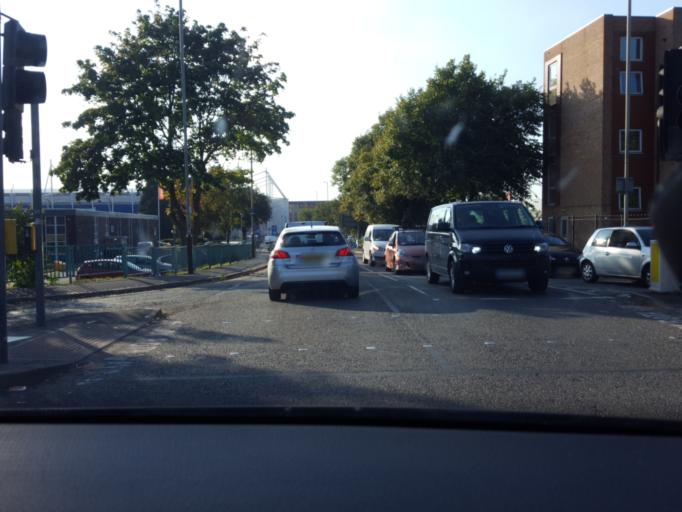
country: GB
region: England
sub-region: City of Leicester
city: Leicester
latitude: 52.6198
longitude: -1.1371
